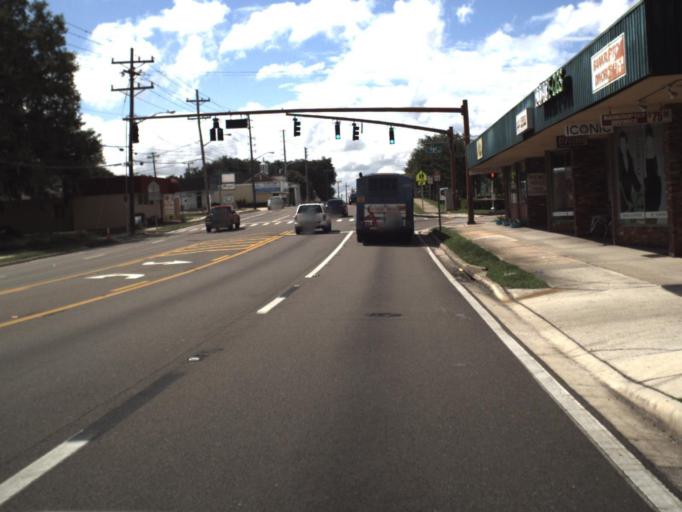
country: US
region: Florida
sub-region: Polk County
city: Lakeland
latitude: 28.0160
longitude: -81.9571
